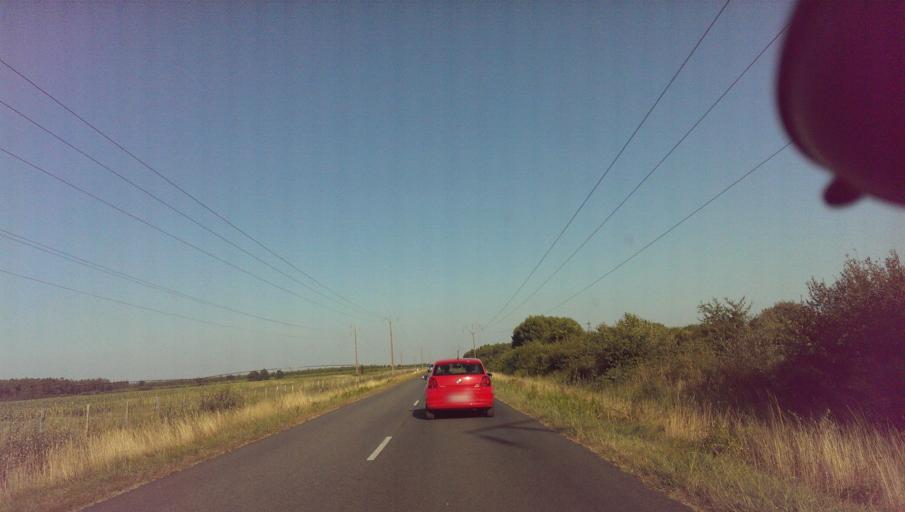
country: FR
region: Aquitaine
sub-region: Departement des Landes
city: Mimizan
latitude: 44.1868
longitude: -1.2034
